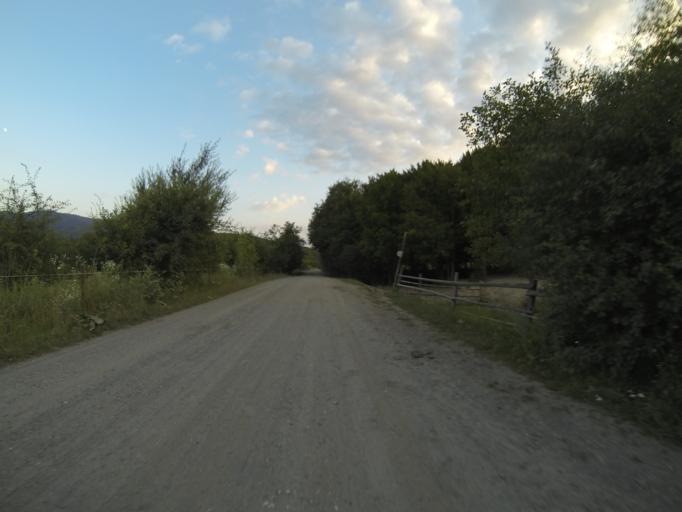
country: RO
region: Brasov
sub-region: Comuna Sinca Noua
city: Sinca Noua
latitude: 45.7396
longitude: 25.2968
